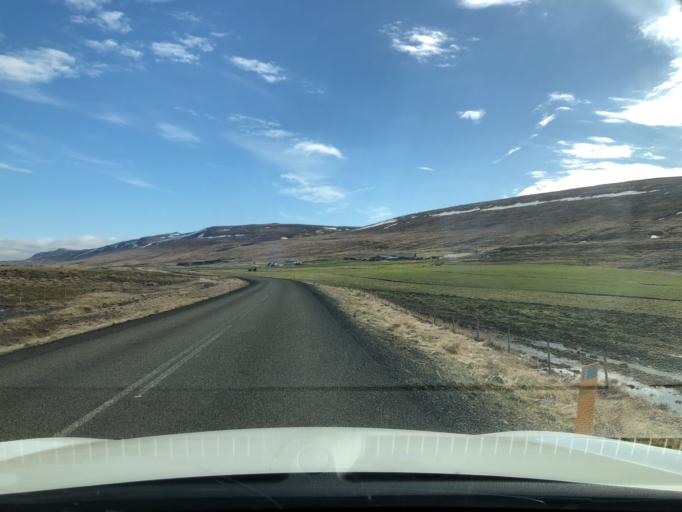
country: IS
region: West
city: Borgarnes
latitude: 65.1262
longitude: -21.6455
